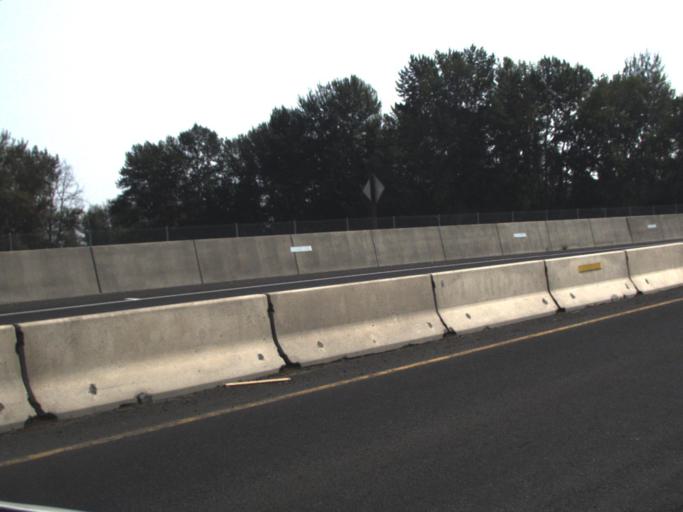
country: US
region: Washington
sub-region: Yakima County
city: Union Gap
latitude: 46.5838
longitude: -120.4652
